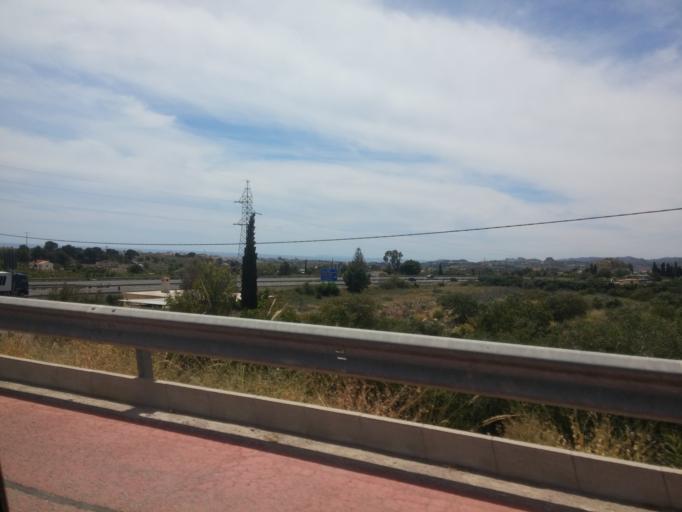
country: ES
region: Valencia
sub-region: Provincia de Alicante
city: Villajoyosa
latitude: 38.5318
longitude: -0.2207
